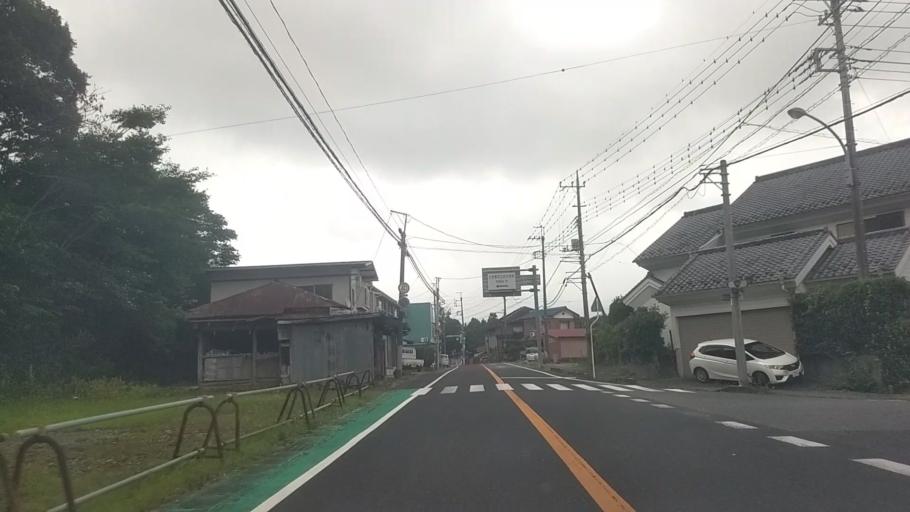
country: JP
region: Chiba
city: Katsuura
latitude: 35.2504
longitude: 140.2014
